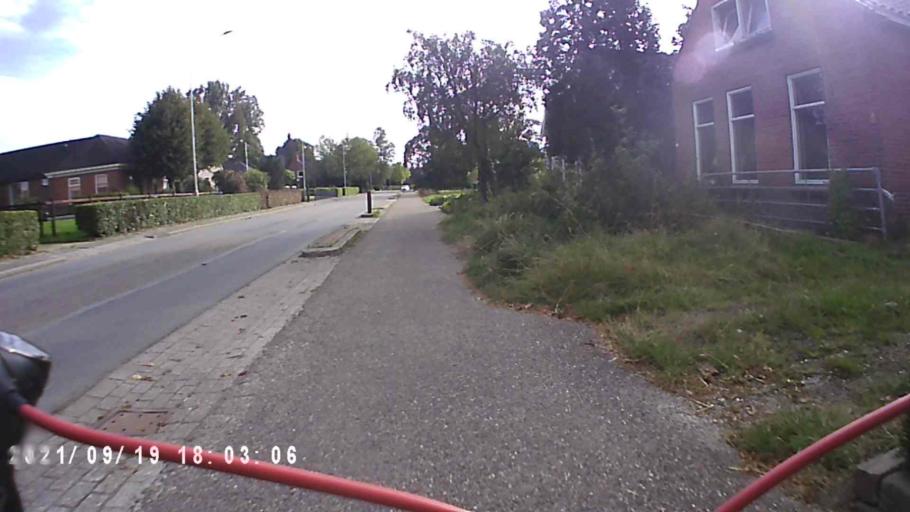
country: NL
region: Groningen
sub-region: Gemeente Delfzijl
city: Delfzijl
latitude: 53.2483
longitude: 6.9276
